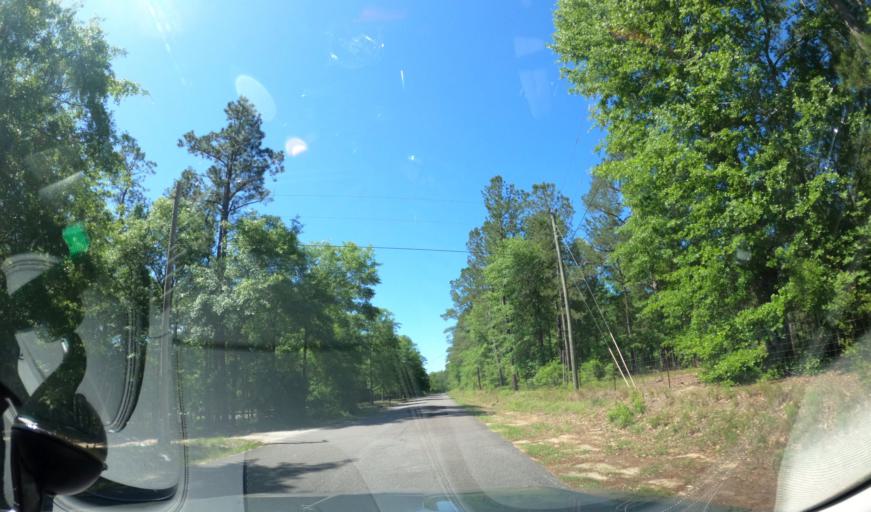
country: US
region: South Carolina
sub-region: Aiken County
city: Burnettown
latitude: 33.4405
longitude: -81.8109
